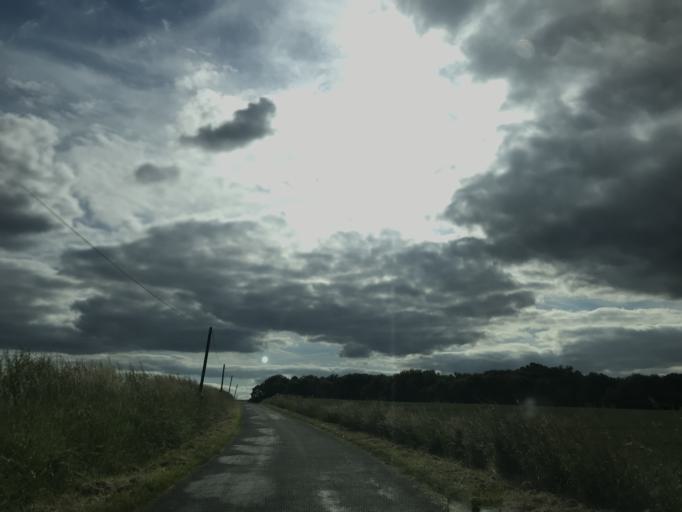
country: FR
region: Aquitaine
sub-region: Departement de la Dordogne
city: Saint-Aulaye
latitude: 45.2502
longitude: 0.1252
